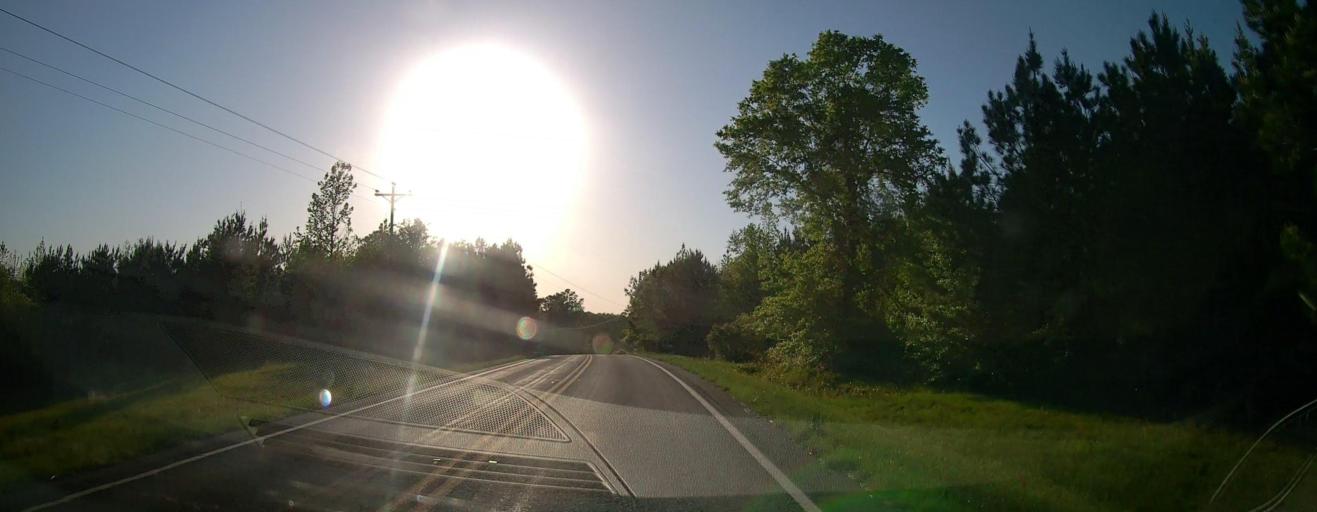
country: US
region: Georgia
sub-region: Macon County
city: Oglethorpe
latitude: 32.3171
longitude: -84.1733
